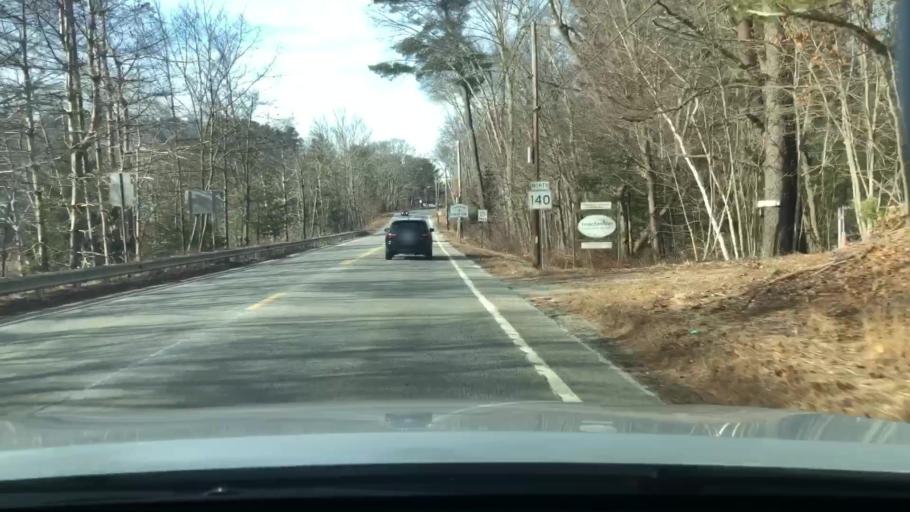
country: US
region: Massachusetts
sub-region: Worcester County
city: Northbridge
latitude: 42.1819
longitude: -71.6444
